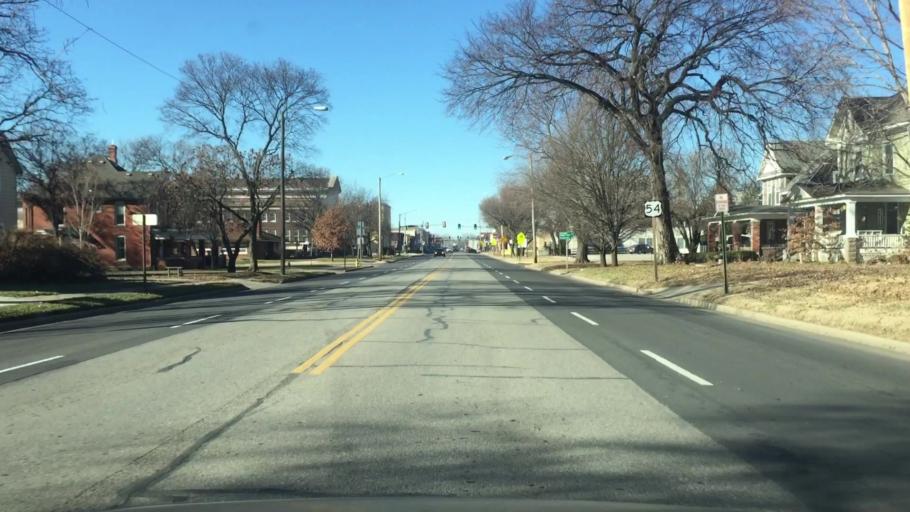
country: US
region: Kansas
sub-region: Allen County
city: Iola
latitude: 37.9214
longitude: -95.3988
